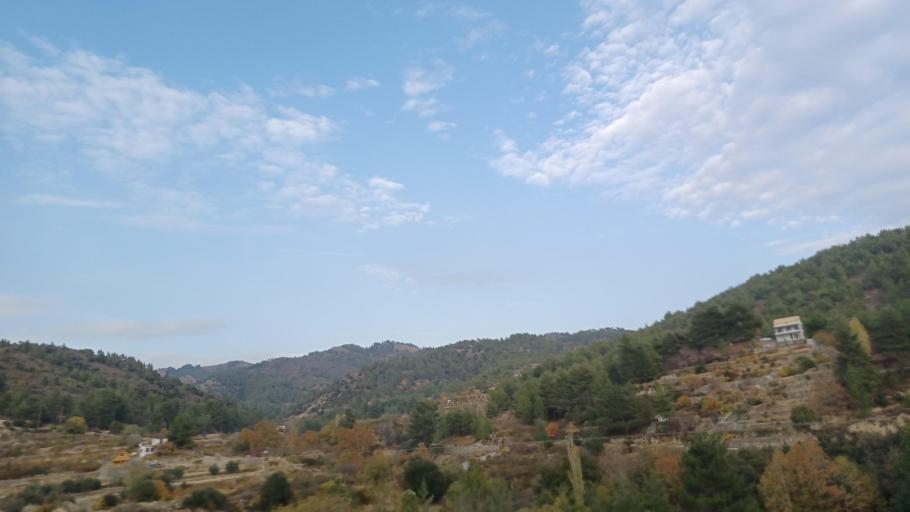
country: CY
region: Limassol
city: Pelendri
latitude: 34.9134
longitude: 32.9413
